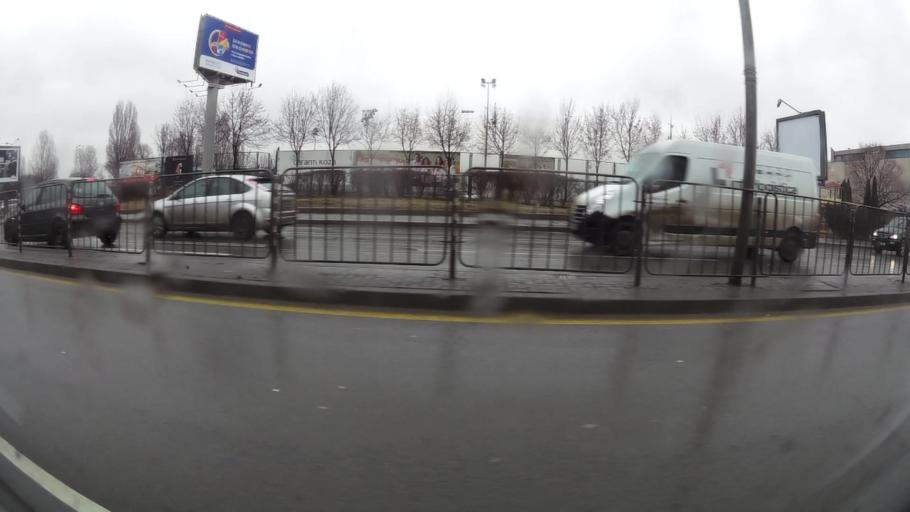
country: BG
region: Sofia-Capital
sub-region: Stolichna Obshtina
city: Sofia
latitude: 42.6530
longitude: 23.3802
